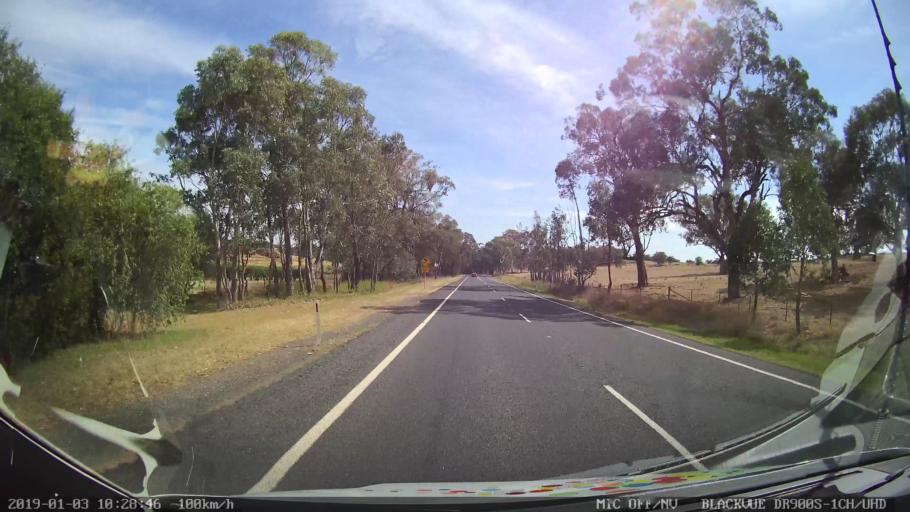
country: AU
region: New South Wales
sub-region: Young
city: Young
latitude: -34.3833
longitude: 148.2597
